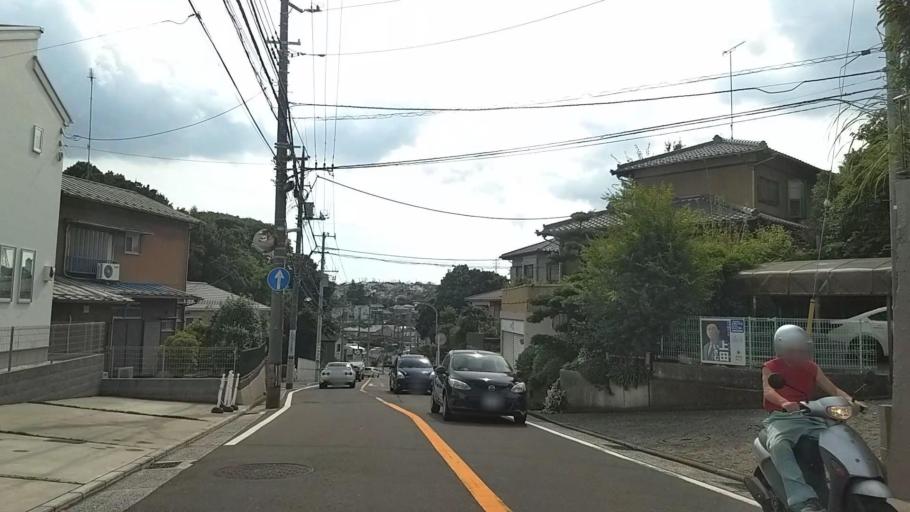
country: JP
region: Kanagawa
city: Yokohama
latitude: 35.4879
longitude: 139.5737
